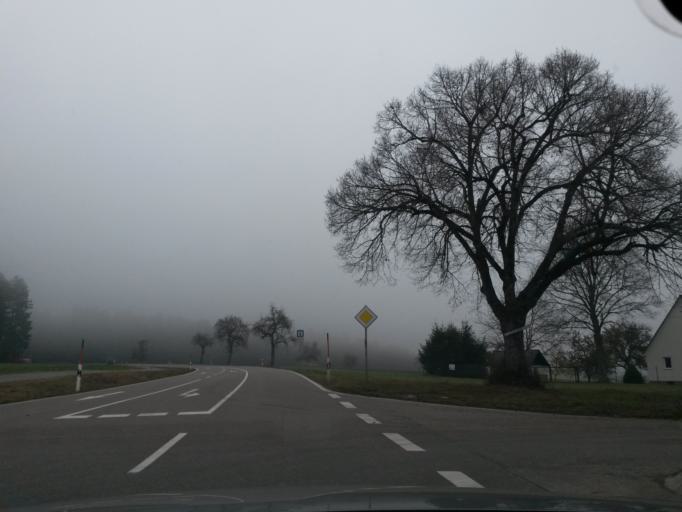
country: DE
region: Baden-Wuerttemberg
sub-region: Freiburg Region
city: Dornhan
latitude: 48.3559
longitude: 8.4673
